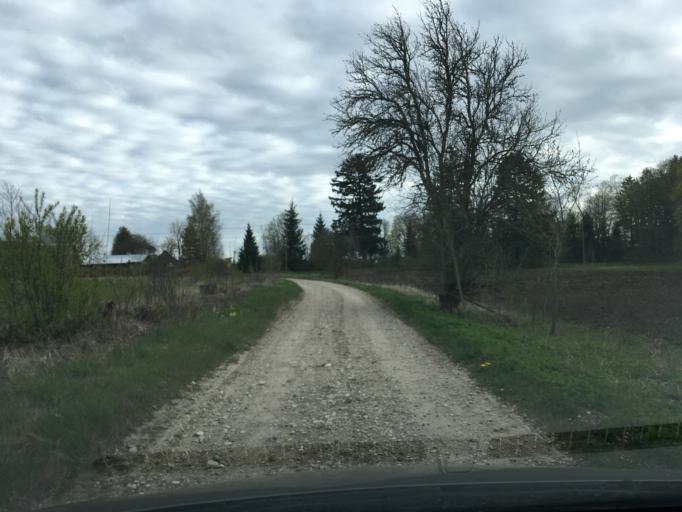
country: EE
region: Laeaene
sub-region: Lihula vald
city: Lihula
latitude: 58.5754
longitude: 23.7237
